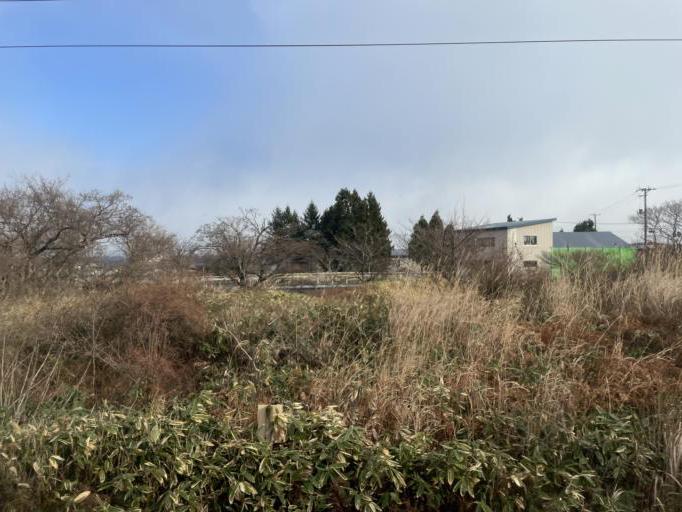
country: JP
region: Aomori
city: Aomori Shi
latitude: 40.9148
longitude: 141.0371
